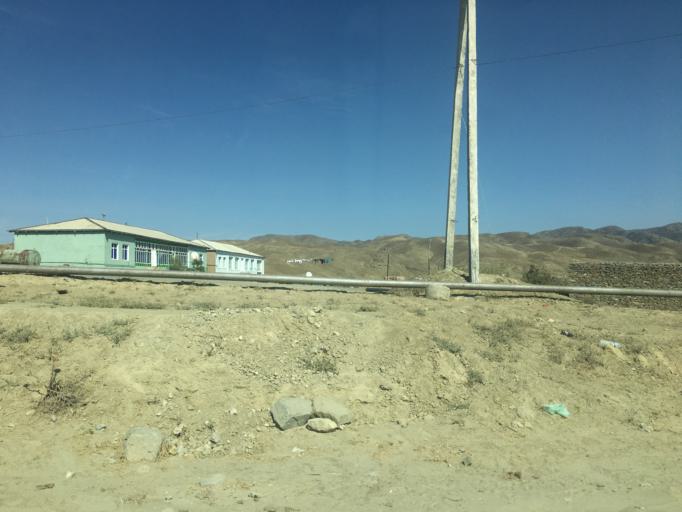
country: TM
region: Ahal
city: Baharly
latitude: 38.3949
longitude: 57.0333
